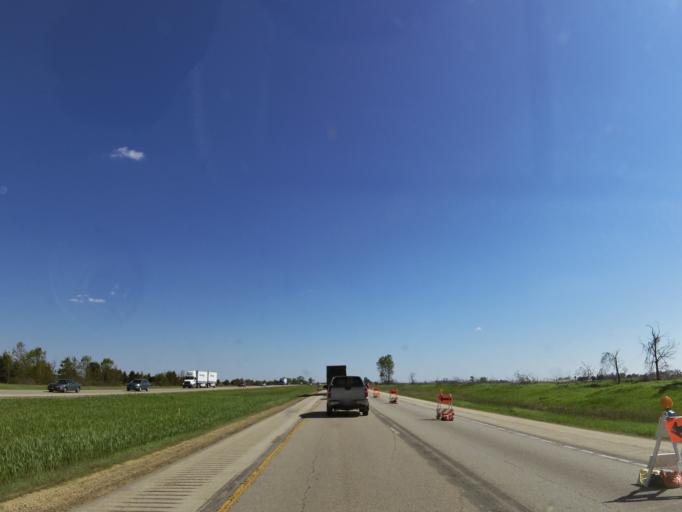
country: US
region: Illinois
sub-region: Ogle County
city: Hillcrest
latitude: 42.0364
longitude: -89.0212
